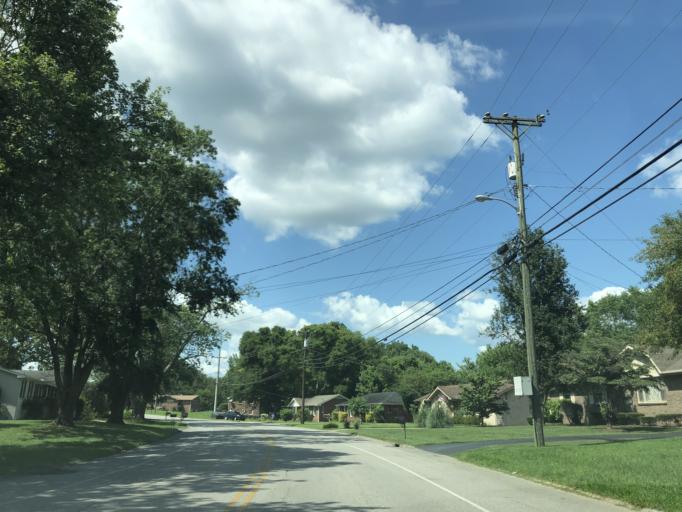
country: US
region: Tennessee
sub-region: Wilson County
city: Green Hill
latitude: 36.2221
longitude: -86.5831
